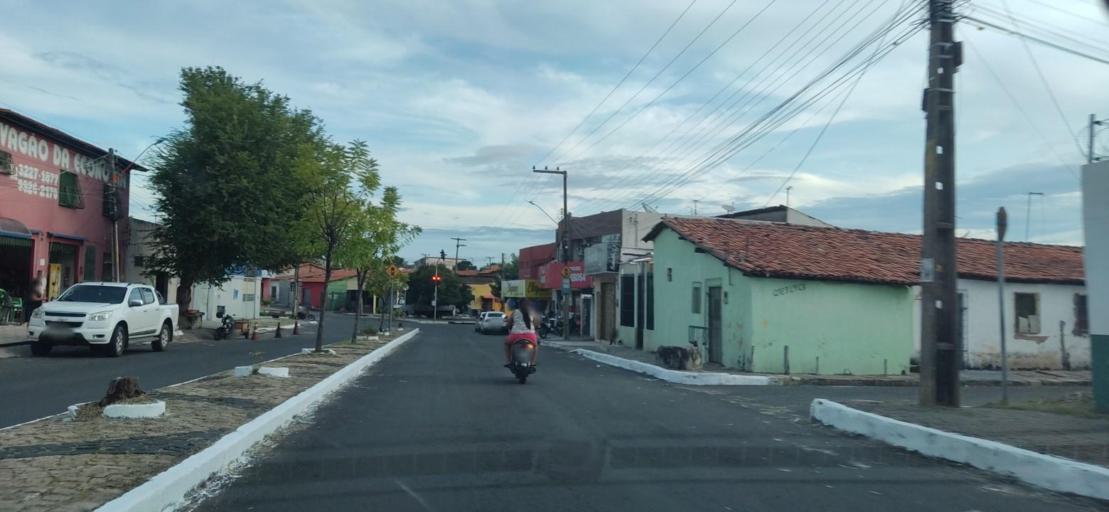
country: BR
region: Piaui
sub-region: Teresina
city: Teresina
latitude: -5.1518
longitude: -42.7876
